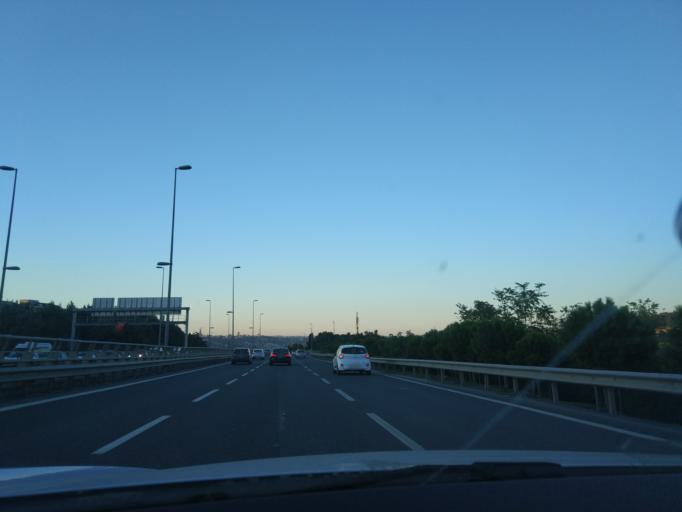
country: TR
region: Istanbul
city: UEskuedar
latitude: 41.0286
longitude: 29.0459
